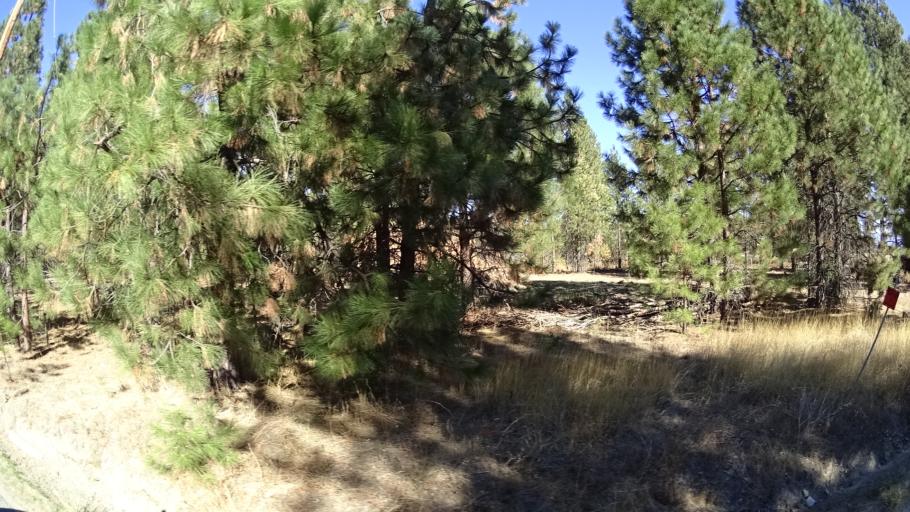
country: US
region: California
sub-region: Siskiyou County
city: Yreka
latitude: 41.5267
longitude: -122.9126
